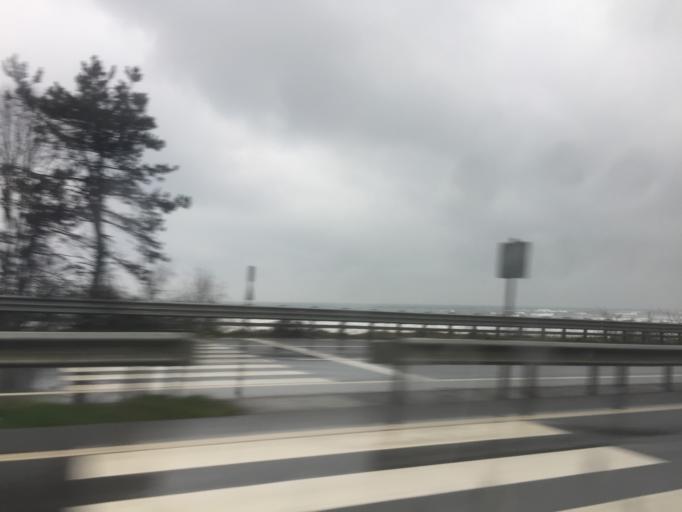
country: TR
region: Zonguldak
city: Alapli
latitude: 41.1166
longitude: 31.2977
